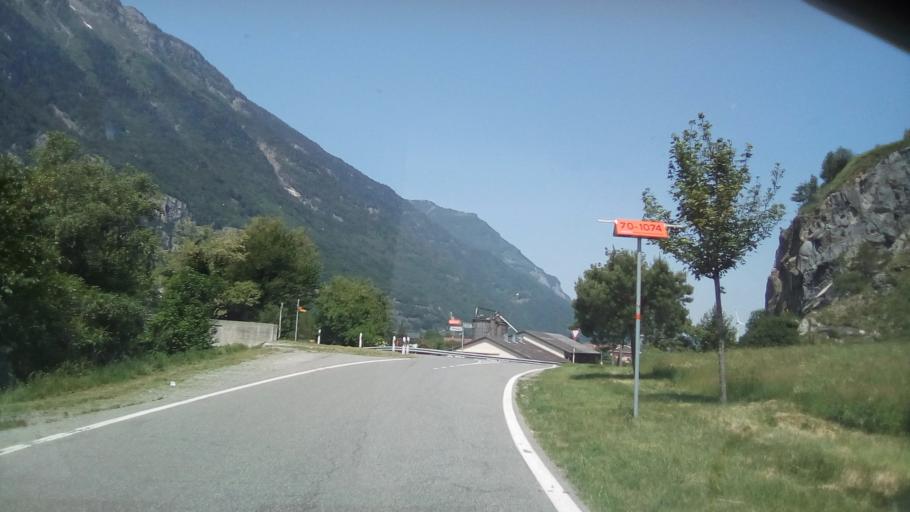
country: CH
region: Valais
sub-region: Saint-Maurice District
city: Vernayaz
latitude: 46.1427
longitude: 7.0463
